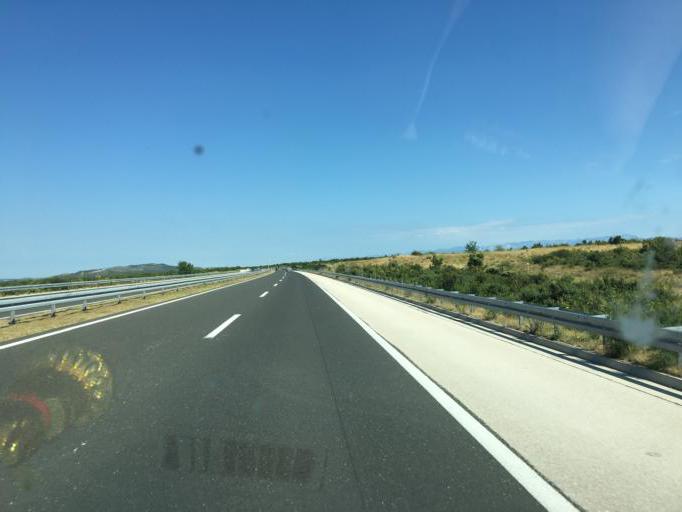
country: HR
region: Zadarska
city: Benkovac
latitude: 44.0299
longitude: 15.5658
